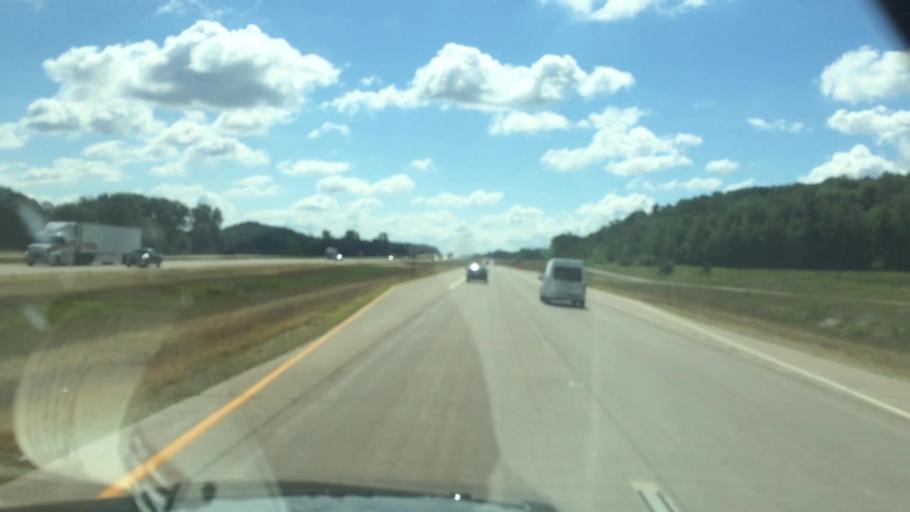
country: US
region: Wisconsin
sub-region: Waupaca County
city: King
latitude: 44.3726
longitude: -89.1562
